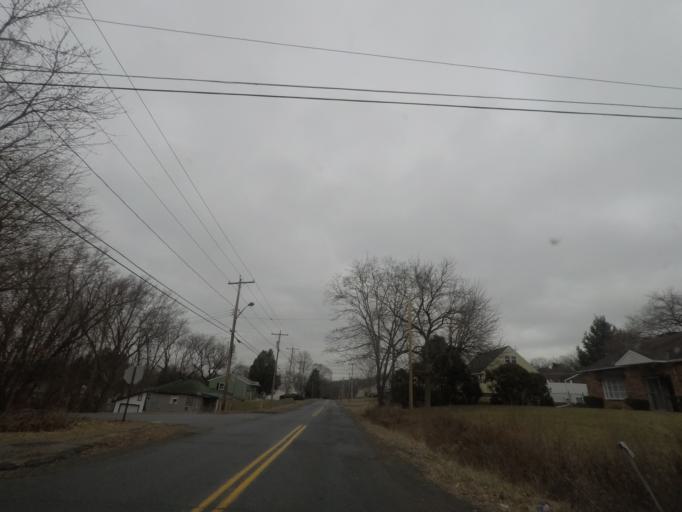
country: US
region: New York
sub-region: Saratoga County
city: Waterford
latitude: 42.7965
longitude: -73.6618
